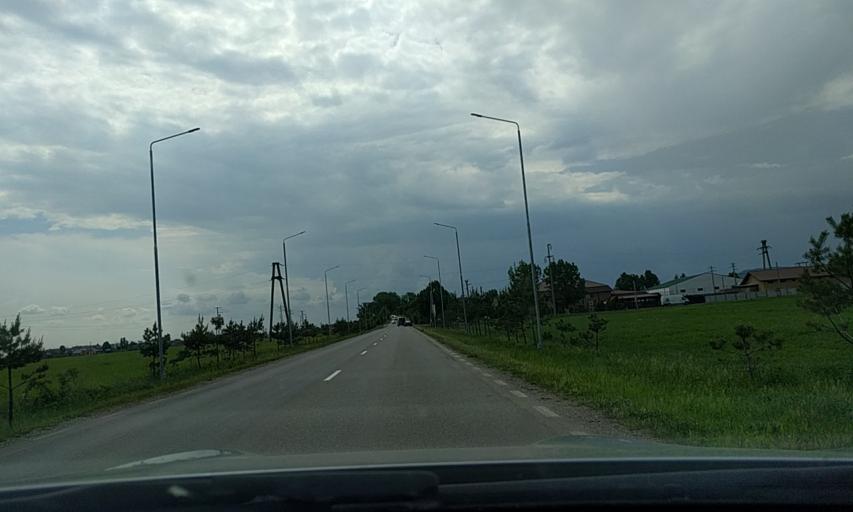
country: RO
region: Prahova
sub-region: Comuna Floresti
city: Floresti
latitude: 45.0368
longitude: 25.8077
